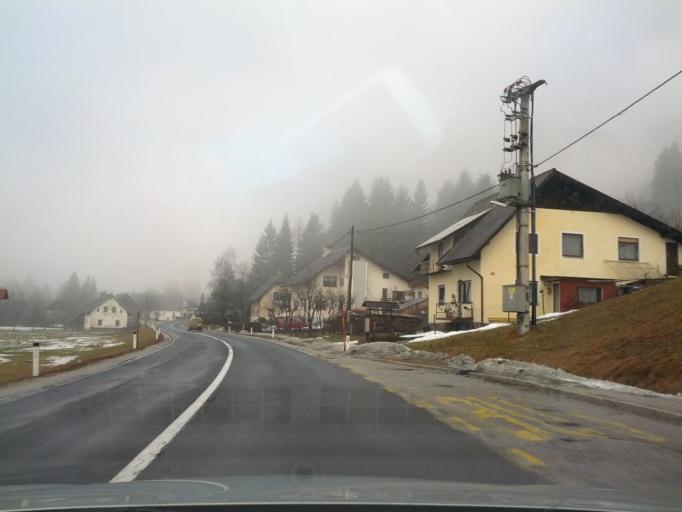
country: SI
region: Kranjska Gora
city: Mojstrana
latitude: 46.4711
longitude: 13.9184
